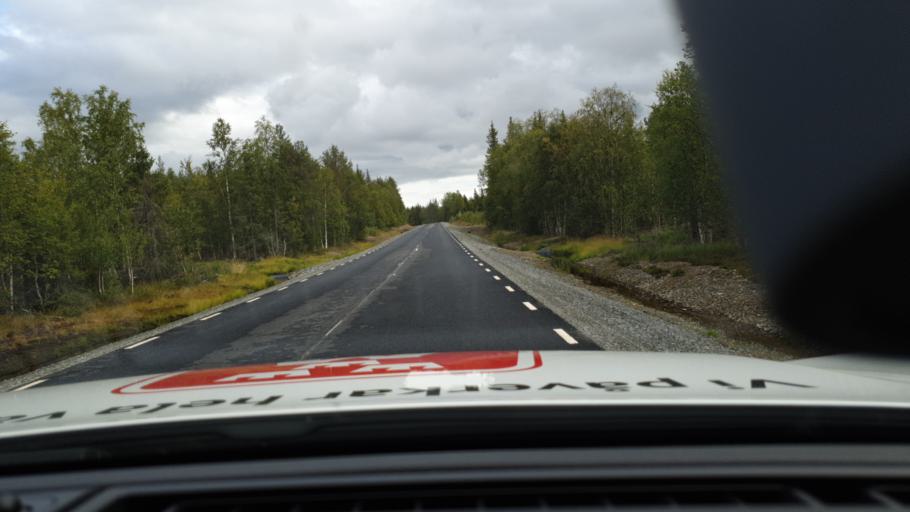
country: SE
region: Norrbotten
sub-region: Gallivare Kommun
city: Gaellivare
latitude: 66.8684
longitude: 21.2088
